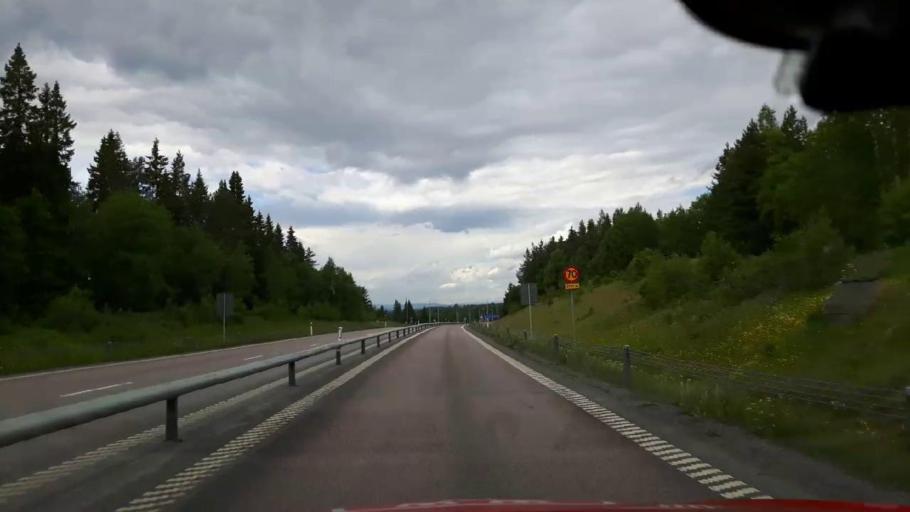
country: SE
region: Jaemtland
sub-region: Krokoms Kommun
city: Krokom
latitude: 63.2646
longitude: 14.5429
